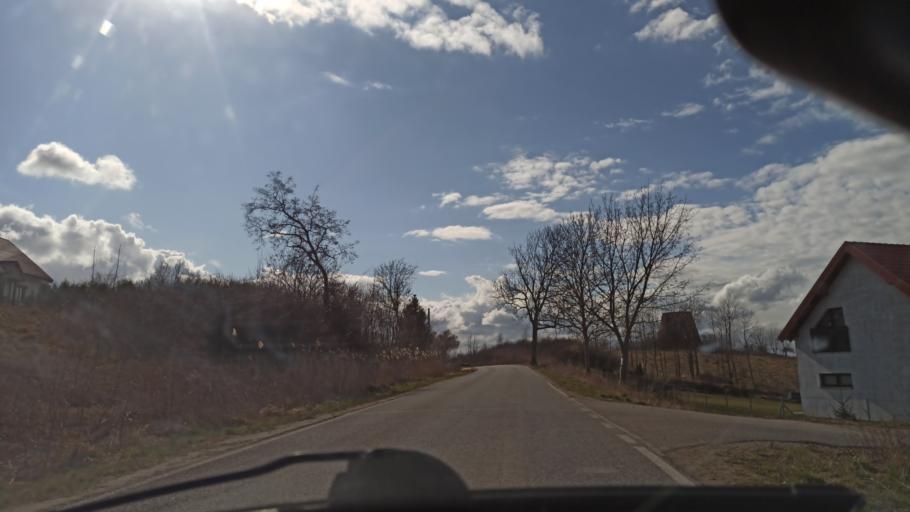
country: PL
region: Warmian-Masurian Voivodeship
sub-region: Powiat elblaski
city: Tolkmicko
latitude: 54.2708
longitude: 19.4778
